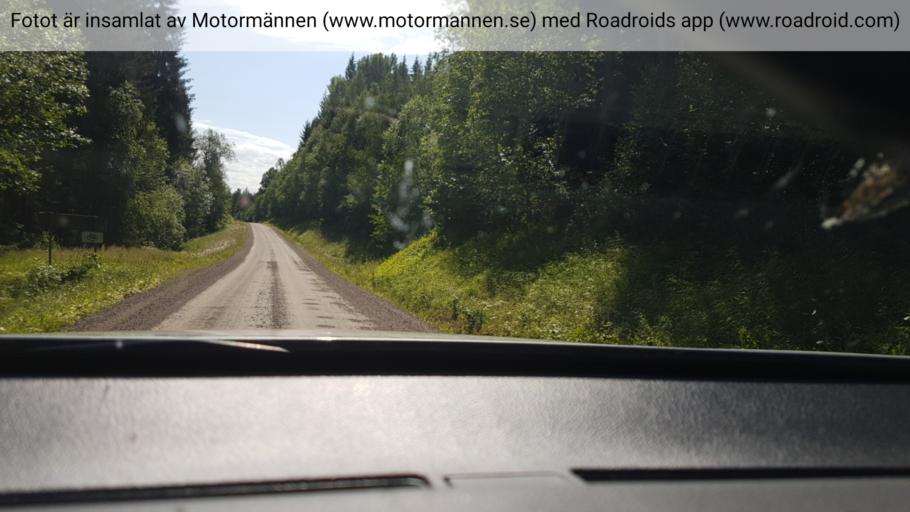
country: SE
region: Vaermland
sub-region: Torsby Kommun
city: Torsby
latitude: 60.5373
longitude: 13.1097
